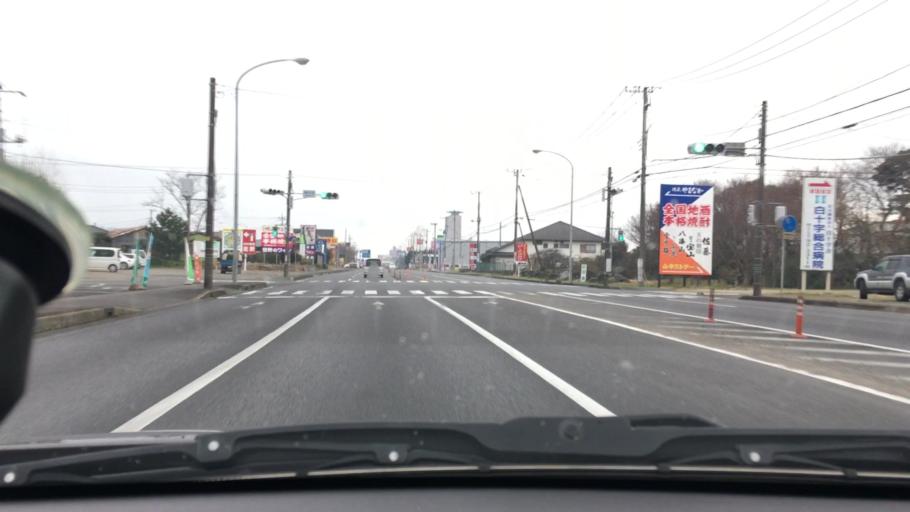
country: JP
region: Chiba
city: Omigawa
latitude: 35.9049
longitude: 140.6272
